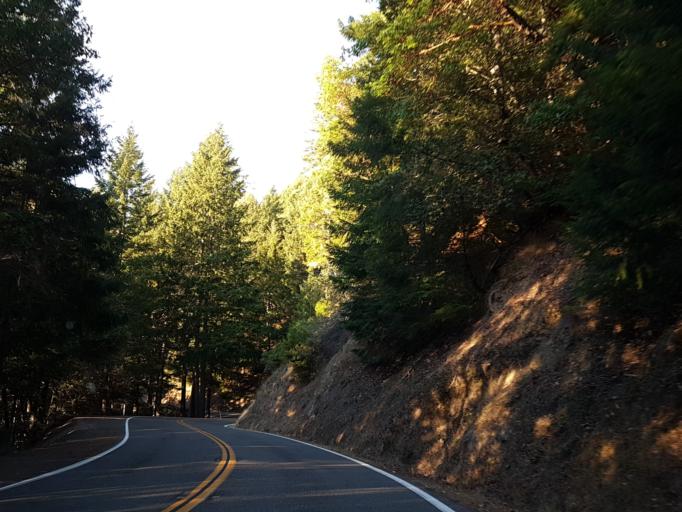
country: US
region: California
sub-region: Humboldt County
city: Redway
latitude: 39.8567
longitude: -123.7442
